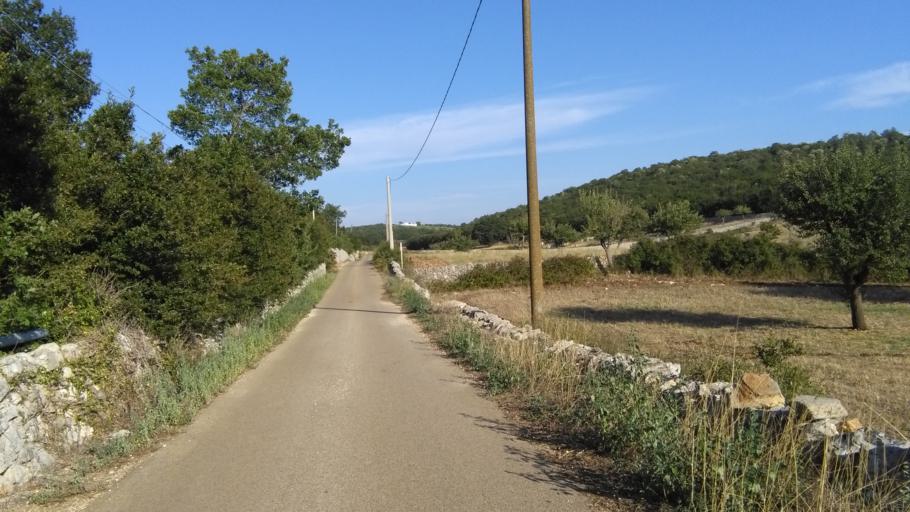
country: IT
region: Apulia
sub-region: Provincia di Bari
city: Putignano
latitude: 40.8303
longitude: 17.0614
